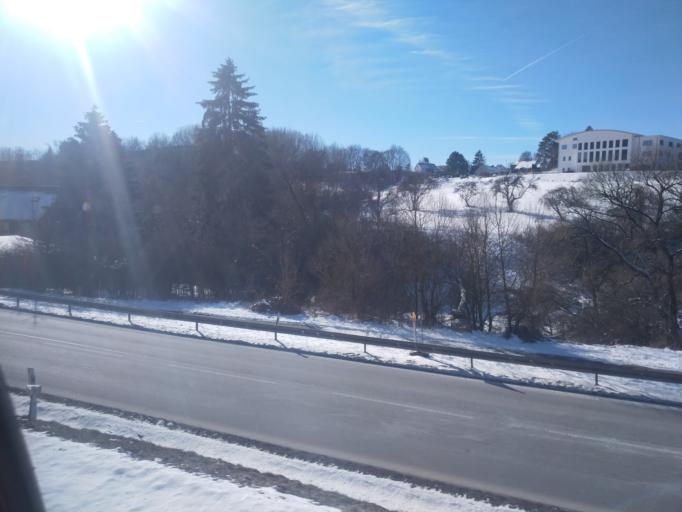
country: DE
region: Baden-Wuerttemberg
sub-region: Freiburg Region
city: Aldingen
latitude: 48.0999
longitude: 8.7072
